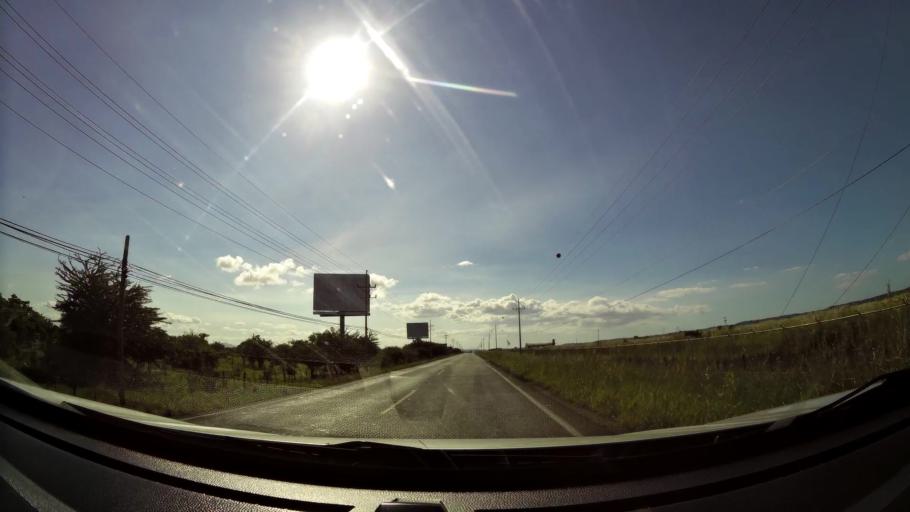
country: CR
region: Guanacaste
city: Liberia
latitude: 10.5897
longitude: -85.5465
